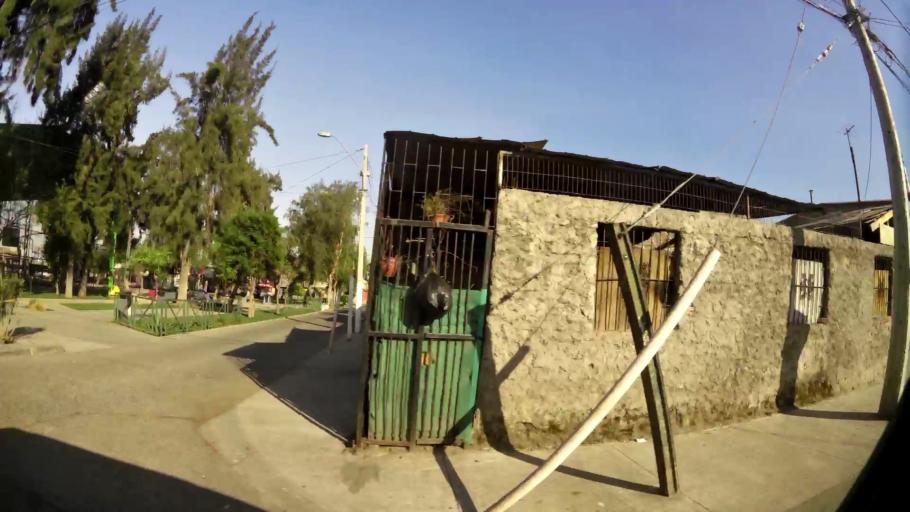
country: CL
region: Santiago Metropolitan
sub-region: Provincia de Santiago
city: Lo Prado
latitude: -33.4400
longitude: -70.7483
